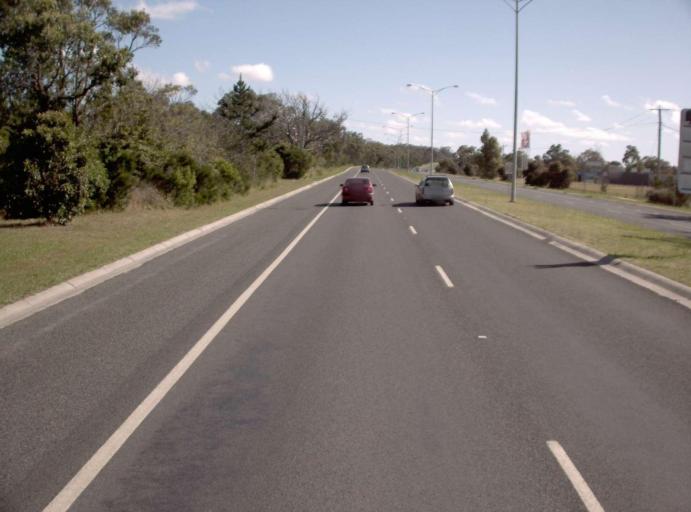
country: AU
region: Victoria
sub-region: Bass Coast
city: North Wonthaggi
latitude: -38.4093
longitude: 145.5292
